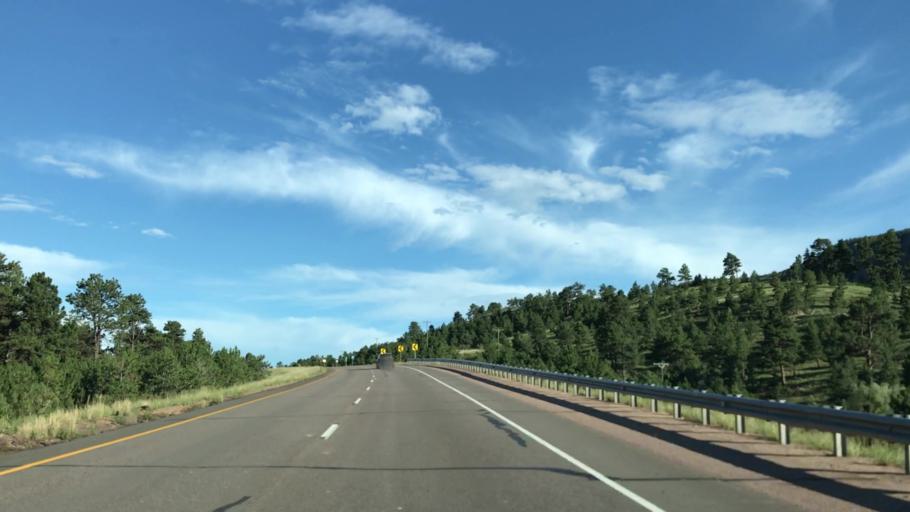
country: US
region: Colorado
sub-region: El Paso County
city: Cascade-Chipita Park
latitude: 38.9376
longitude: -105.0109
